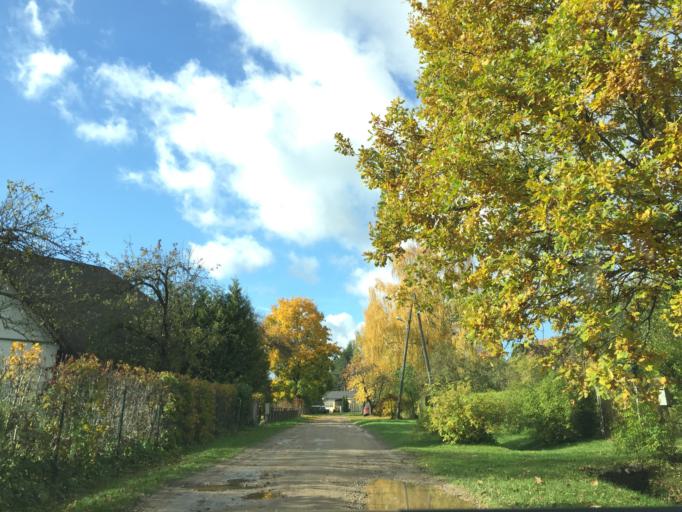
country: LV
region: Lielvarde
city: Lielvarde
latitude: 56.7168
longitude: 24.7962
